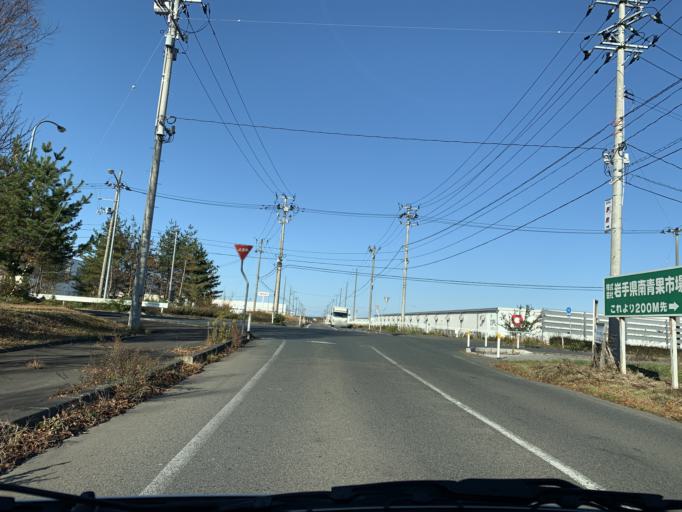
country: JP
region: Iwate
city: Kitakami
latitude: 39.2385
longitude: 141.0839
